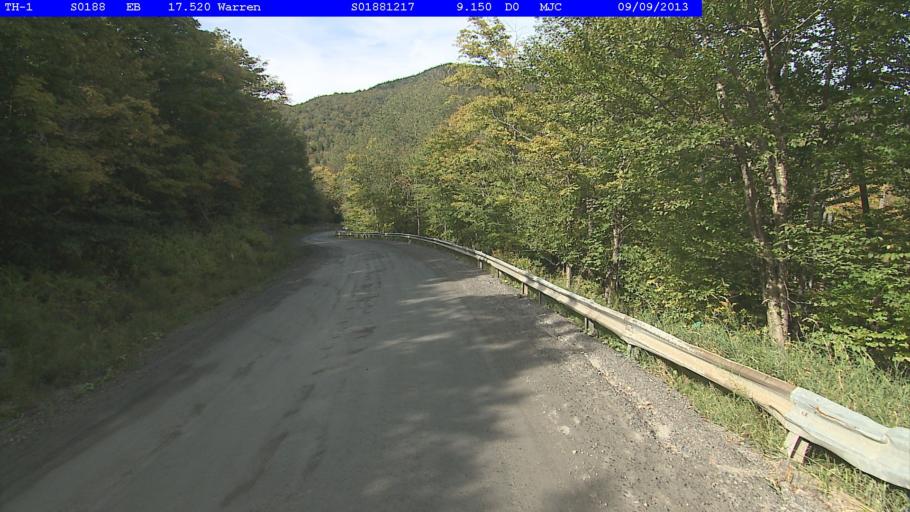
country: US
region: Vermont
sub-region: Washington County
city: Northfield
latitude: 44.1116
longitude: -72.7835
